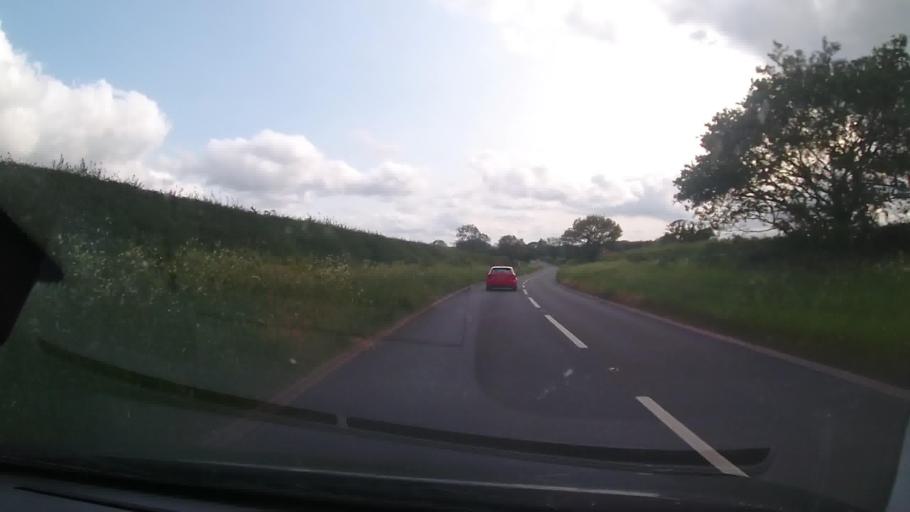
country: GB
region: England
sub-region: Shropshire
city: Clive
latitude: 52.8032
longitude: -2.7523
